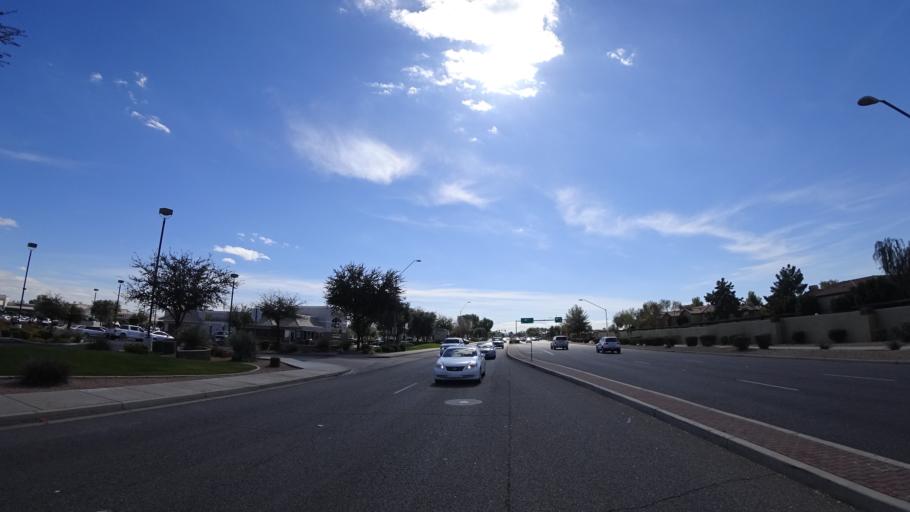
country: US
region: Arizona
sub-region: Maricopa County
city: Peoria
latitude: 33.6707
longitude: -112.2030
